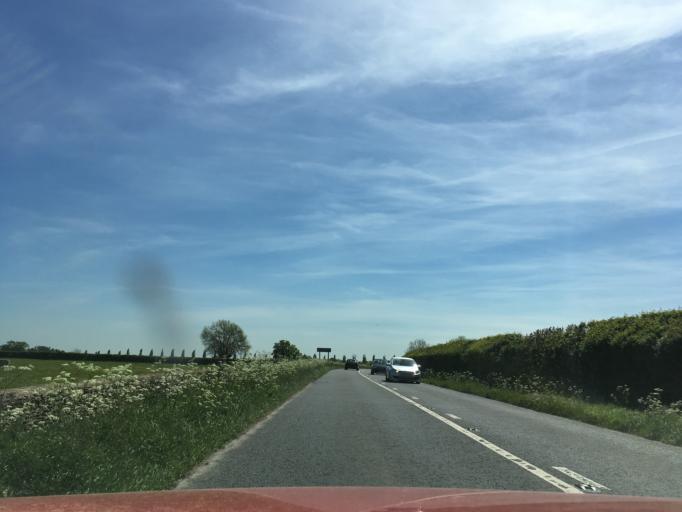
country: GB
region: England
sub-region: Wiltshire
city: Hankerton
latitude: 51.6259
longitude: -2.0753
